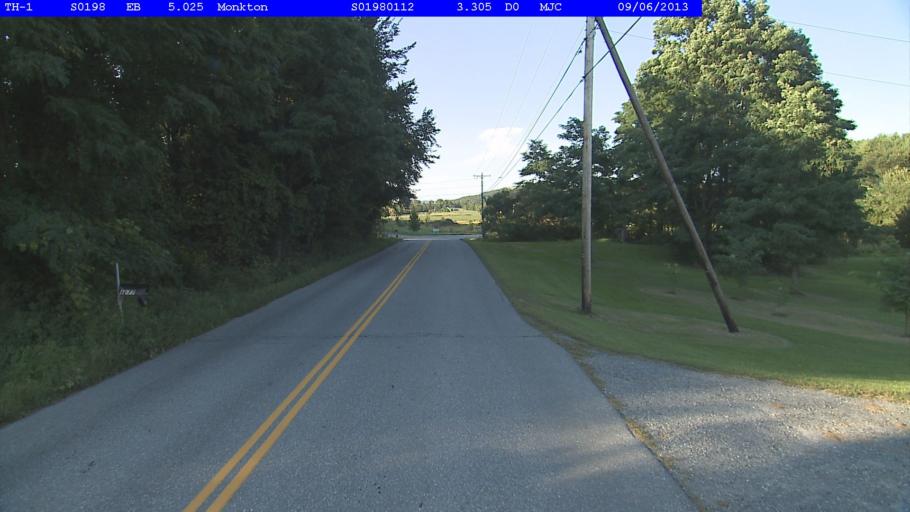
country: US
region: Vermont
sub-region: Chittenden County
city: Hinesburg
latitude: 44.2410
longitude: -73.1429
